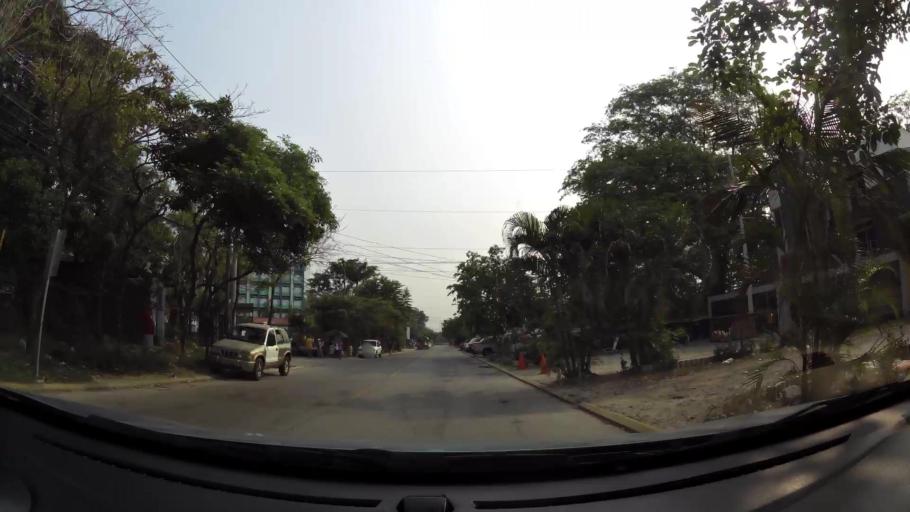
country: HN
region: Cortes
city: El Zapotal del Norte
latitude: 15.5226
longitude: -88.0412
